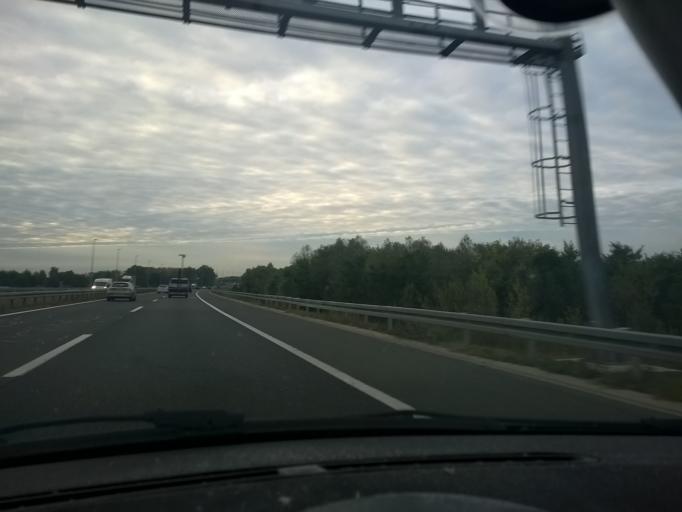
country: HR
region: Grad Zagreb
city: Jezdovec
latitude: 45.7962
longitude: 15.8446
